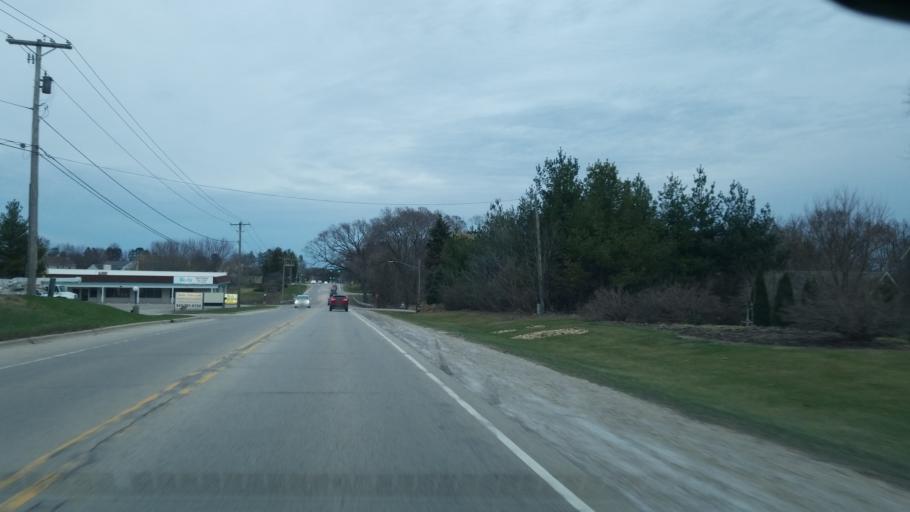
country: US
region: Illinois
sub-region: Kane County
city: Sleepy Hollow
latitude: 42.1008
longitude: -88.3065
